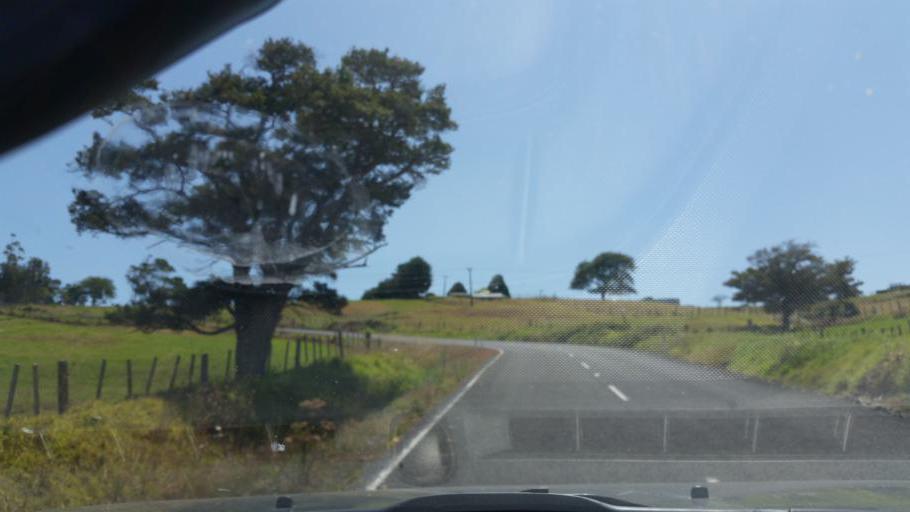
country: NZ
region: Northland
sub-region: Kaipara District
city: Dargaville
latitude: -36.0064
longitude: 173.9562
